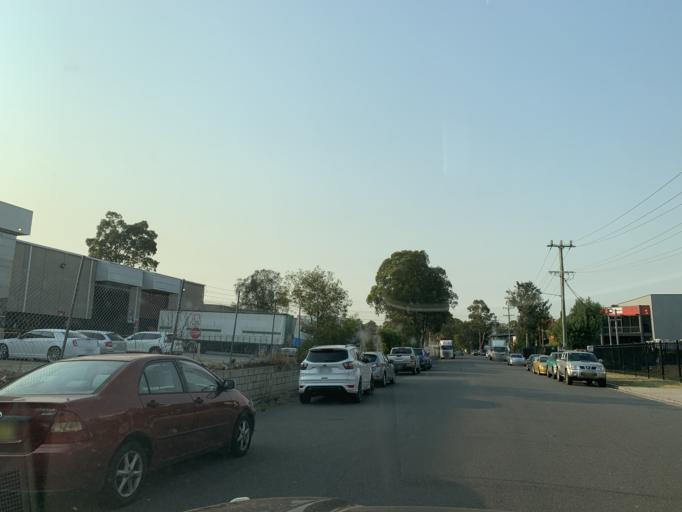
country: AU
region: New South Wales
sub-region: Fairfield
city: Horsley Park
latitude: -33.8389
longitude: 150.8856
